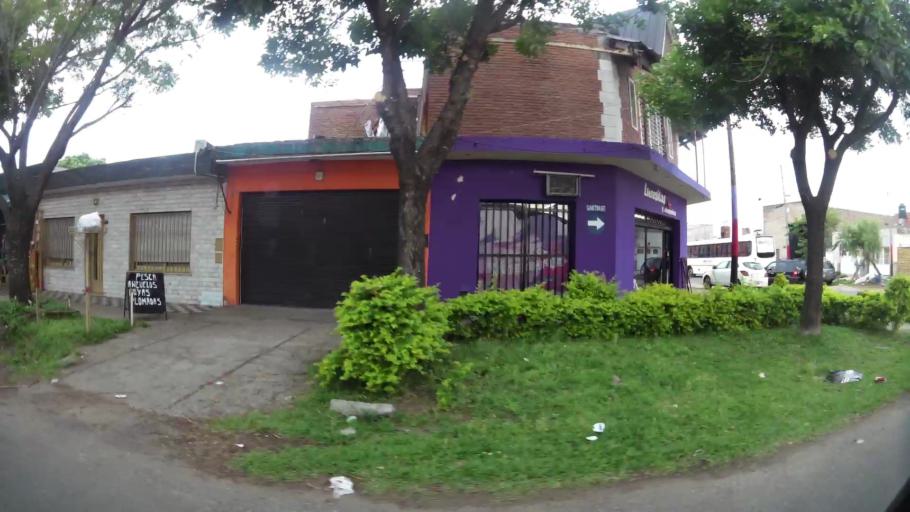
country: AR
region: Santa Fe
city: Gobernador Galvez
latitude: -32.9976
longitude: -60.6679
